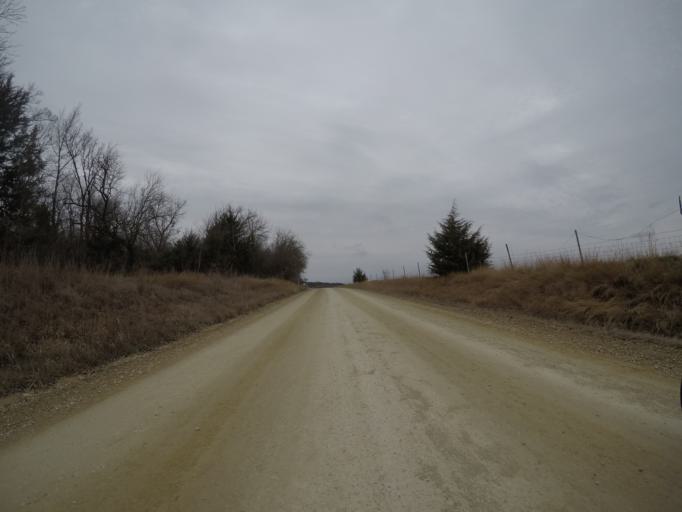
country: US
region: Kansas
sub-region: Riley County
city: Ogden
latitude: 39.1537
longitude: -96.6819
